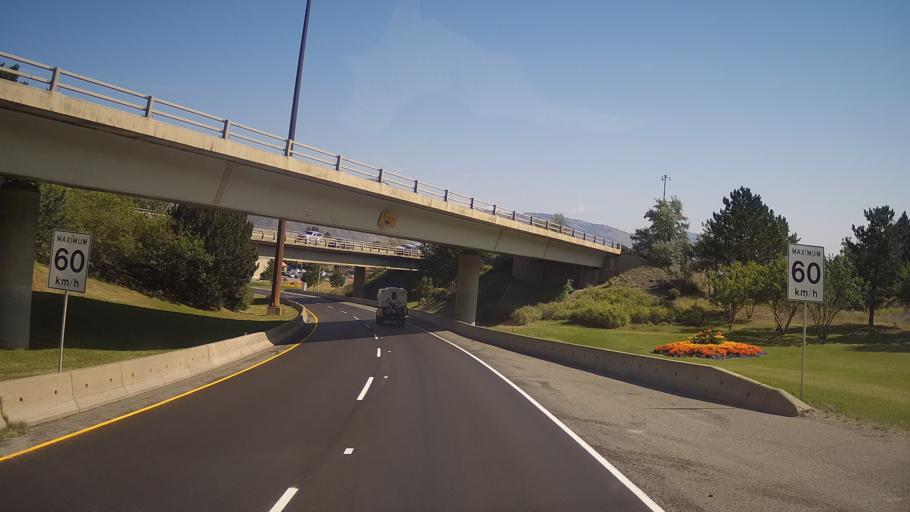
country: CA
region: British Columbia
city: Kamloops
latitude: 50.6607
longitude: -120.3557
